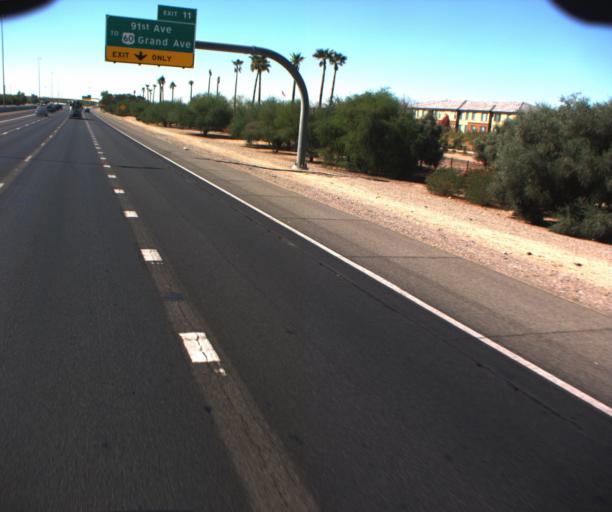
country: US
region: Arizona
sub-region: Maricopa County
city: Sun City
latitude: 33.6069
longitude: -112.2483
